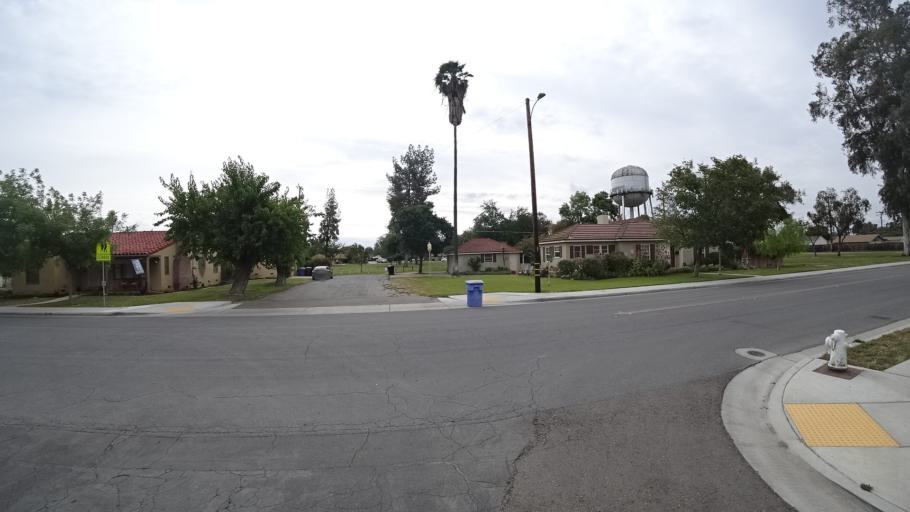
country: US
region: California
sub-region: Kings County
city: Hanford
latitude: 36.3417
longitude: -119.6445
